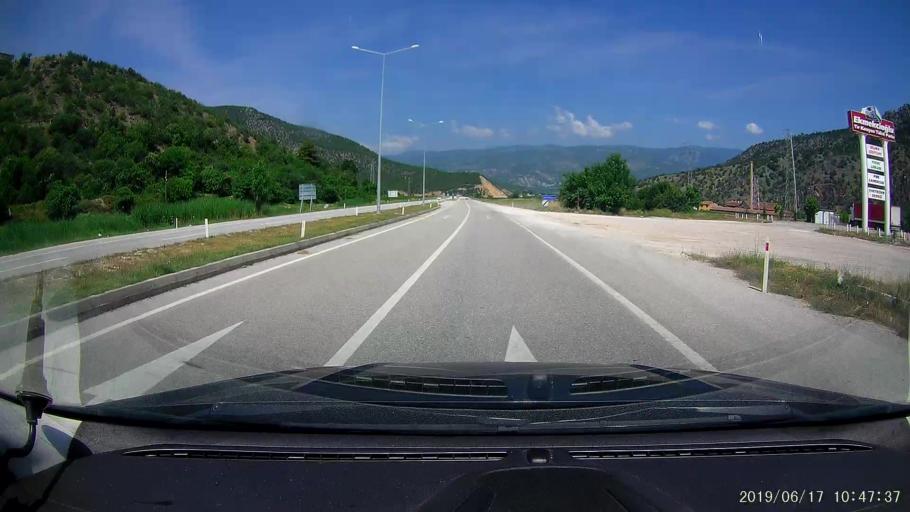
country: TR
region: Corum
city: Hacihamza
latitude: 41.0790
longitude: 34.4459
